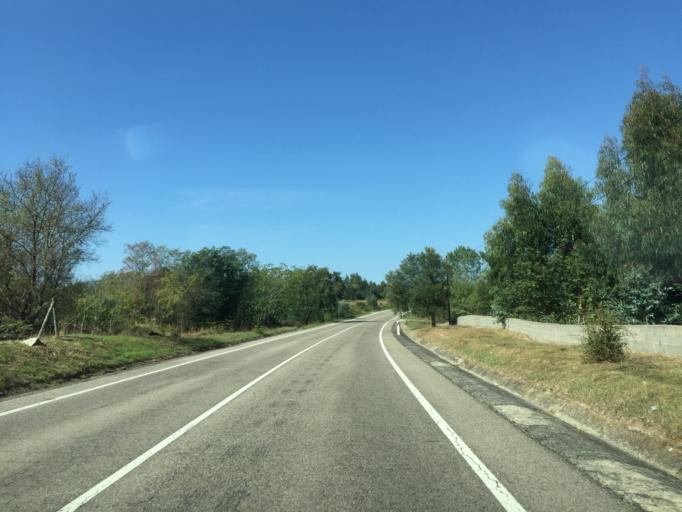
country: PT
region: Portalegre
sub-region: Castelo de Vide
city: Castelo de Vide
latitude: 39.4285
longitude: -7.4950
